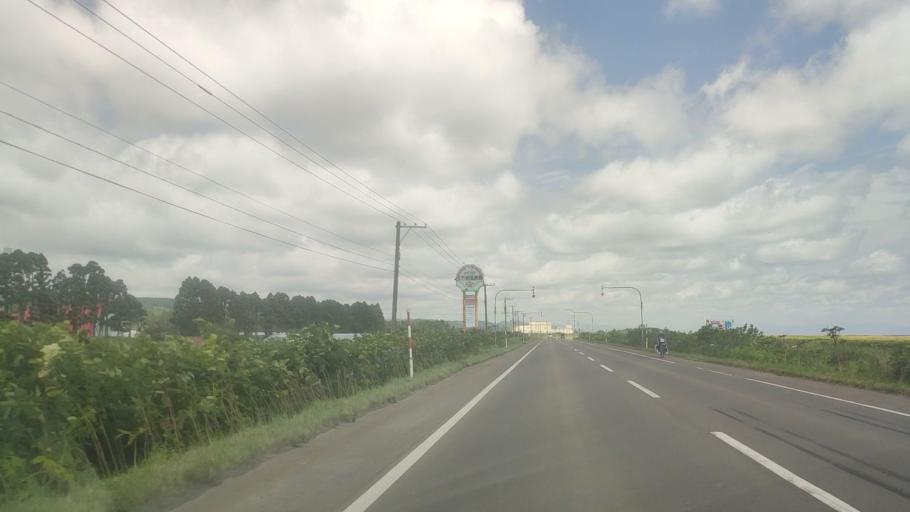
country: JP
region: Hokkaido
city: Niseko Town
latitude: 42.3787
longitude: 140.2927
